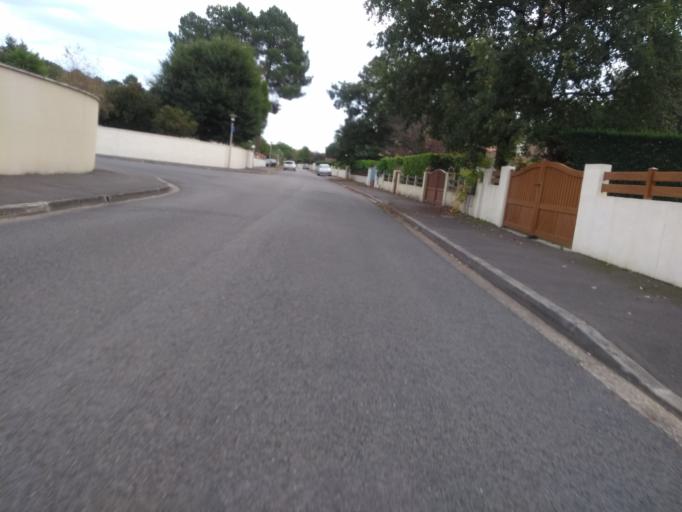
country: FR
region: Aquitaine
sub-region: Departement de la Gironde
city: Cestas
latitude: 44.7342
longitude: -0.6778
